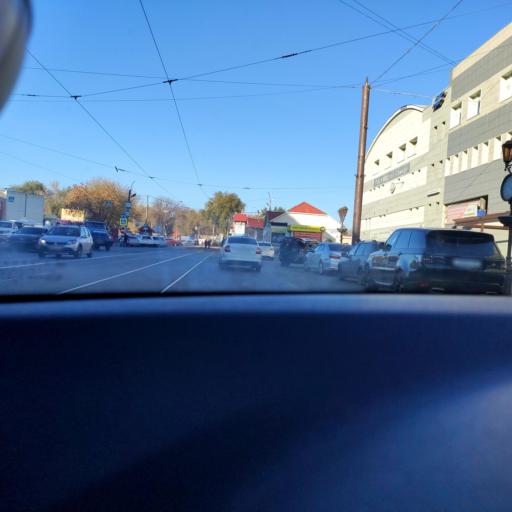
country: RU
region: Samara
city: Petra-Dubrava
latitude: 53.2405
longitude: 50.2769
